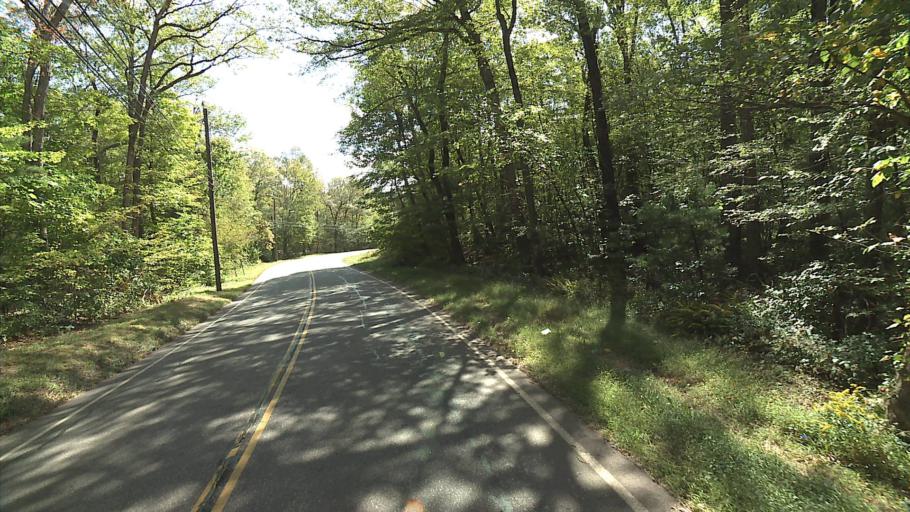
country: US
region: Connecticut
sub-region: Middlesex County
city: Durham
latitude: 41.5332
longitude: -72.7301
